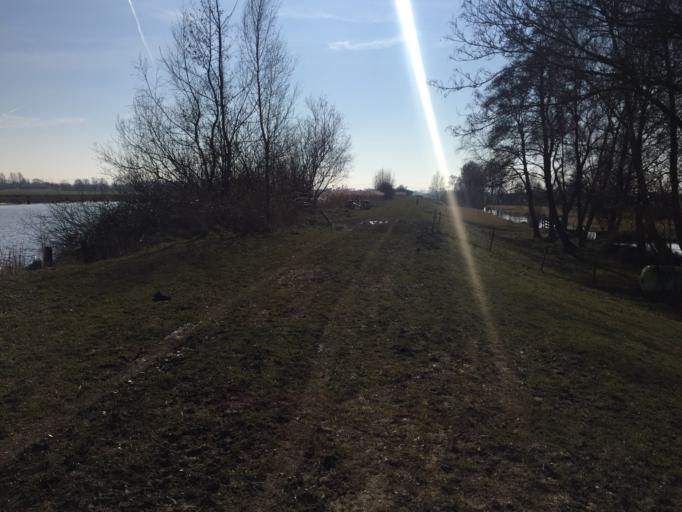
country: NL
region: South Holland
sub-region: Gemeente Vlist
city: Haastrecht
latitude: 52.0309
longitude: 4.7892
